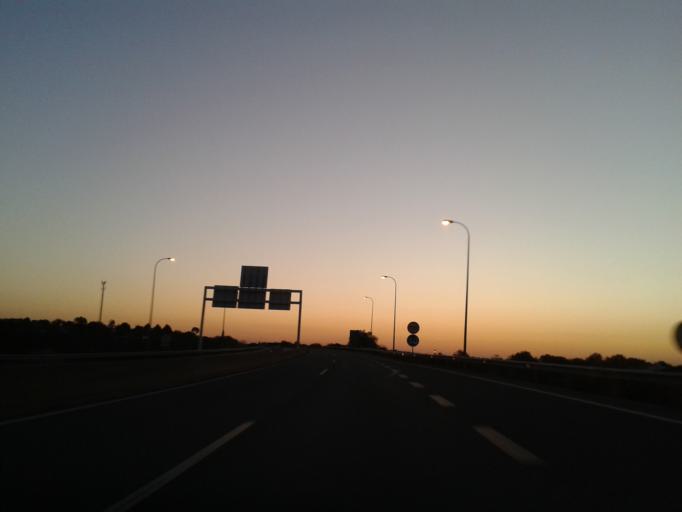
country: PT
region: Faro
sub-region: Albufeira
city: Ferreiras
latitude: 37.1357
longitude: -8.2513
